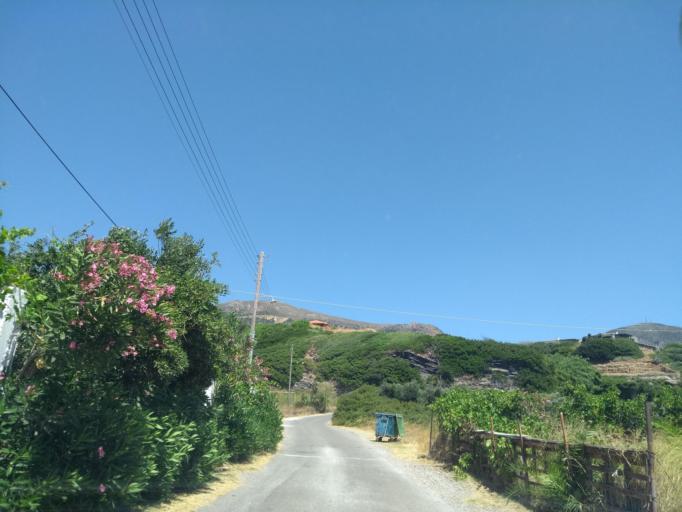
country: GR
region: Crete
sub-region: Nomos Chanias
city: Vryses
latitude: 35.3605
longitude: 23.5319
